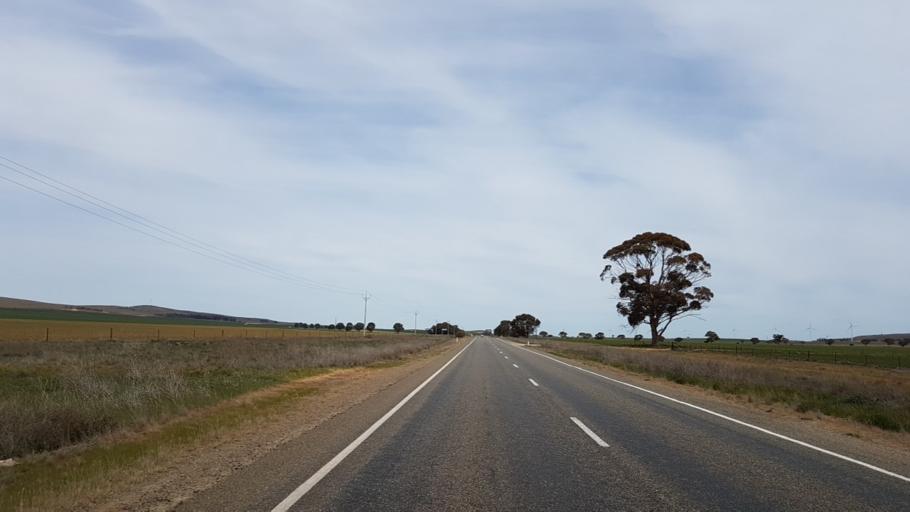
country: AU
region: South Australia
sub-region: Northern Areas
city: Jamestown
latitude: -33.0698
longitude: 138.6161
